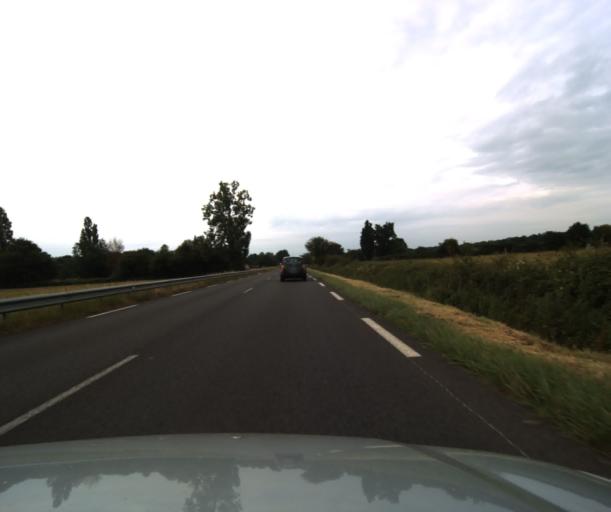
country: FR
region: Midi-Pyrenees
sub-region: Departement des Hautes-Pyrenees
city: Rabastens-de-Bigorre
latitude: 43.3441
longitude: 0.1343
